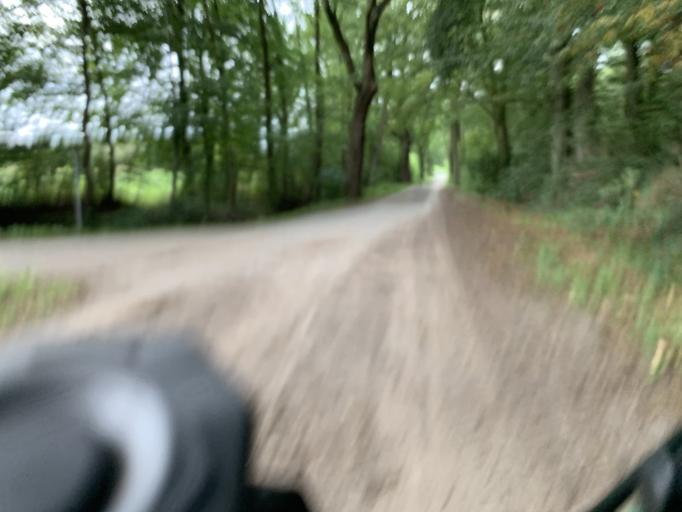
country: DE
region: Lower Saxony
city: Westerstede
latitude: 53.2367
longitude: 7.9152
